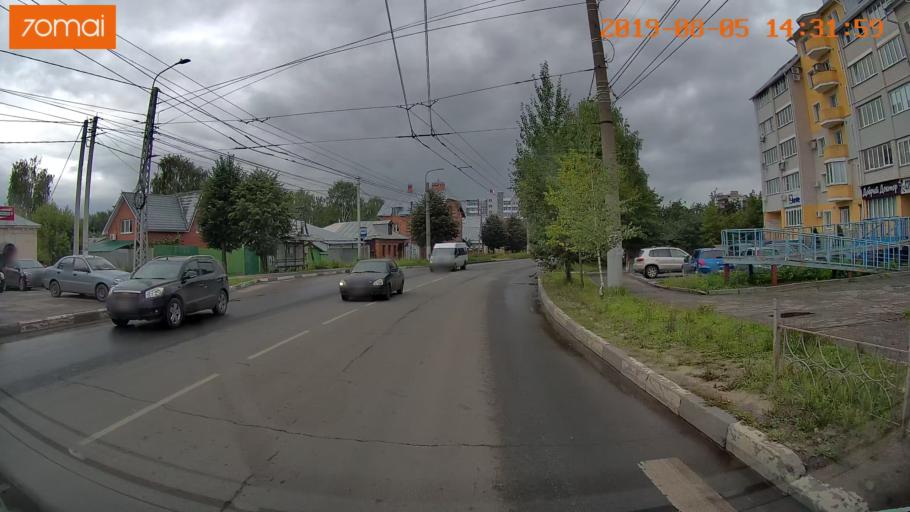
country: RU
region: Ivanovo
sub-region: Gorod Ivanovo
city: Ivanovo
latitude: 56.9894
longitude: 40.9947
